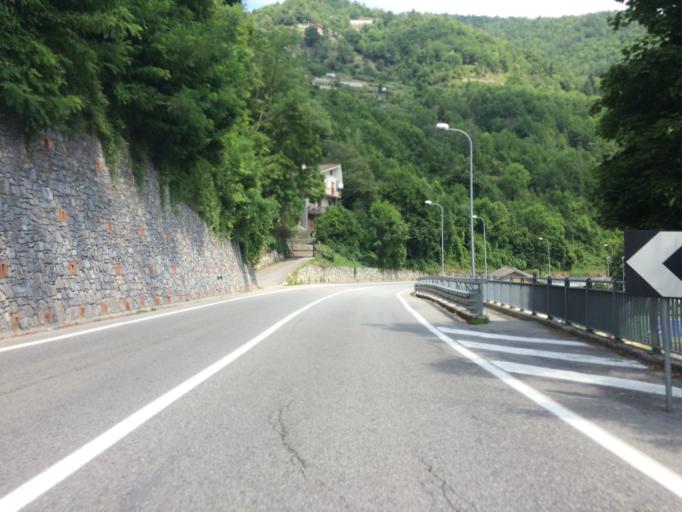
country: IT
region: Piedmont
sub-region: Provincia di Cuneo
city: Ormea
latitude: 44.1526
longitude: 7.9122
